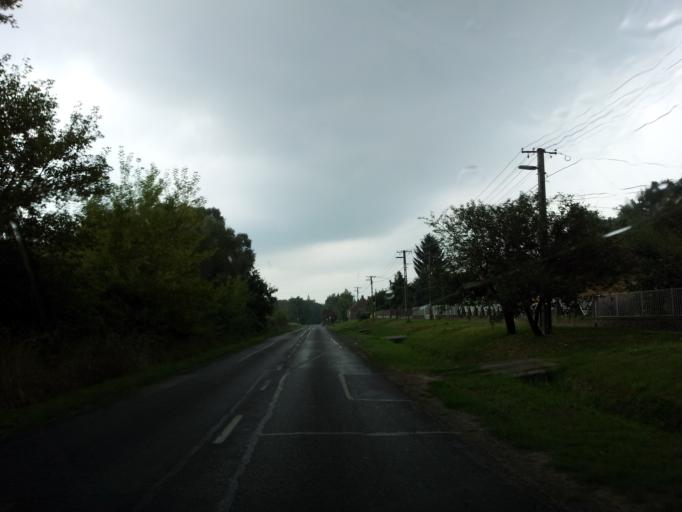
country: HU
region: Tolna
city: Hogyesz
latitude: 46.5044
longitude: 18.4118
